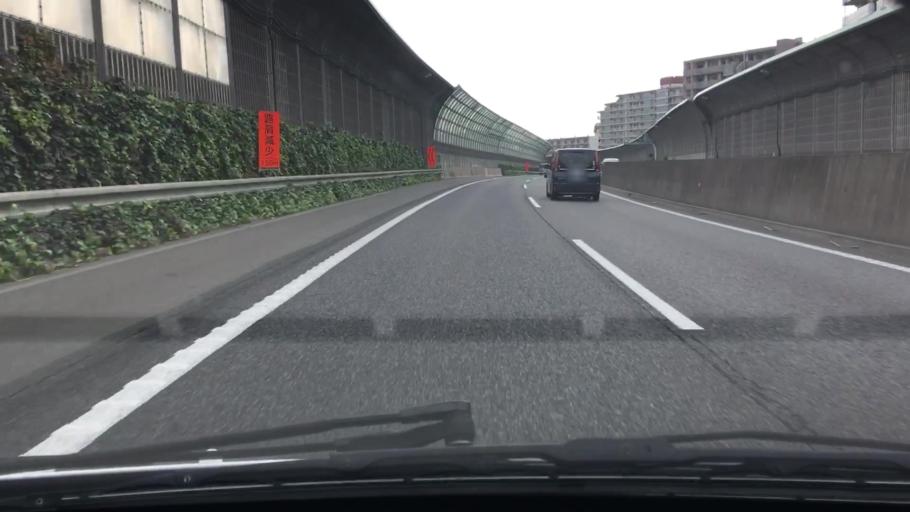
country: JP
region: Chiba
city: Funabashi
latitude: 35.6799
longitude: 140.0115
